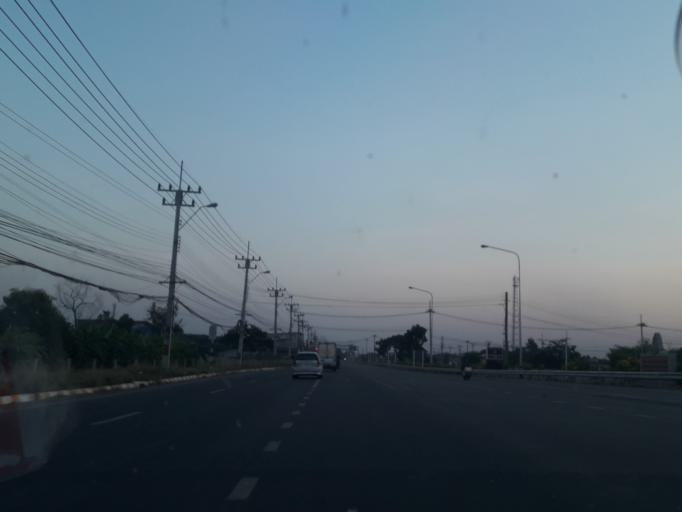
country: TH
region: Pathum Thani
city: Thanyaburi
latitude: 14.0715
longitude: 100.7102
